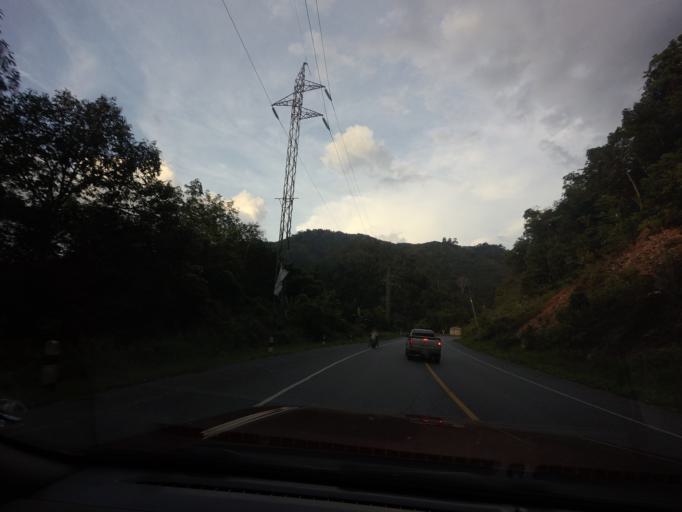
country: TH
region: Yala
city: Than To
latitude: 5.9946
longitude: 101.1919
